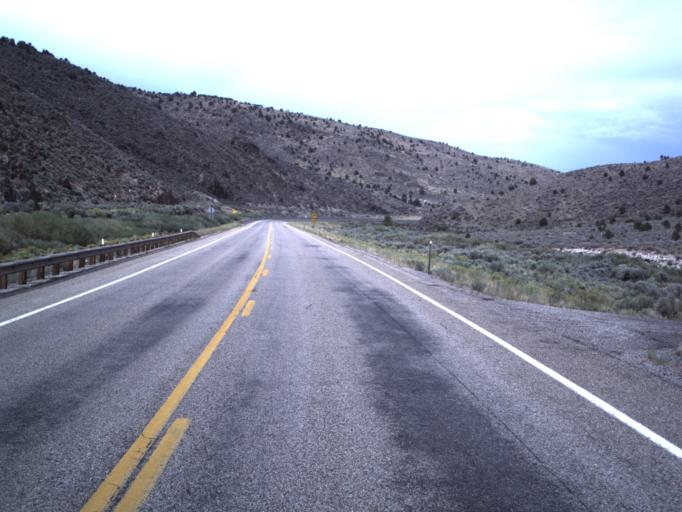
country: US
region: Utah
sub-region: Piute County
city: Junction
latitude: 38.1332
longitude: -112.3158
